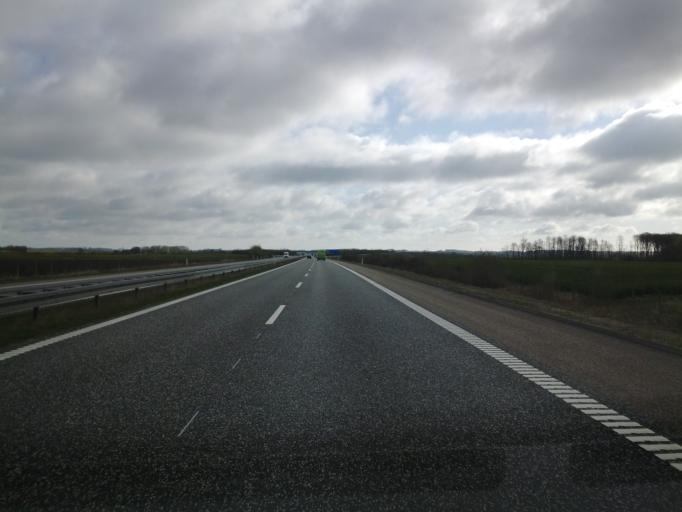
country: DK
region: North Denmark
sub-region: Bronderslev Kommune
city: Dronninglund
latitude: 57.2444
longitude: 10.3188
